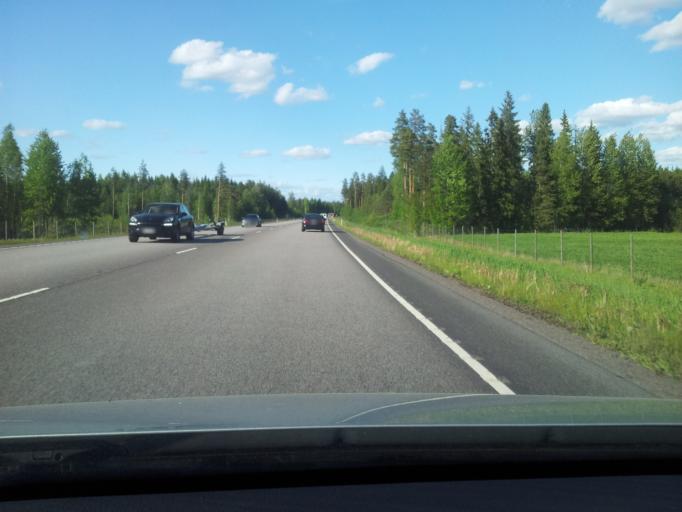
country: FI
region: Uusimaa
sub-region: Loviisa
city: Lapinjaervi
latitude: 60.6805
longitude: 26.2590
